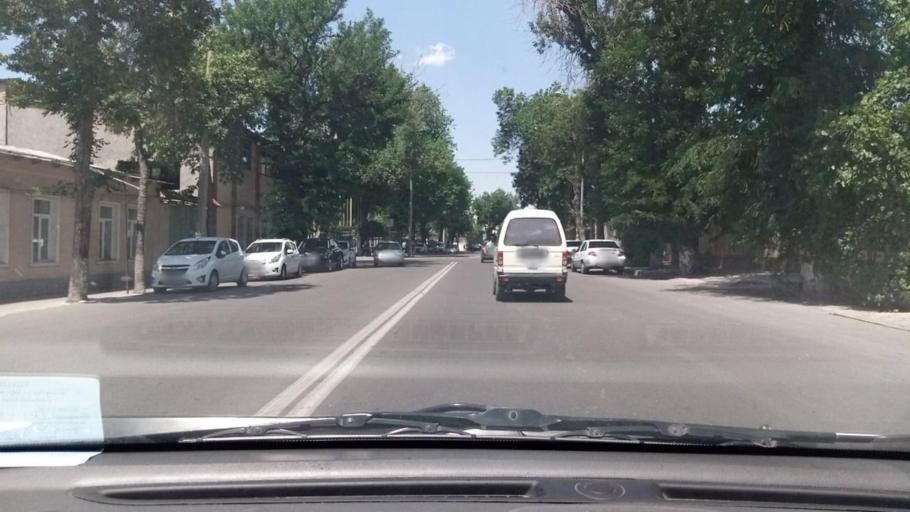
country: UZ
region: Toshkent Shahri
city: Tashkent
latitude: 41.2754
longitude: 69.2755
